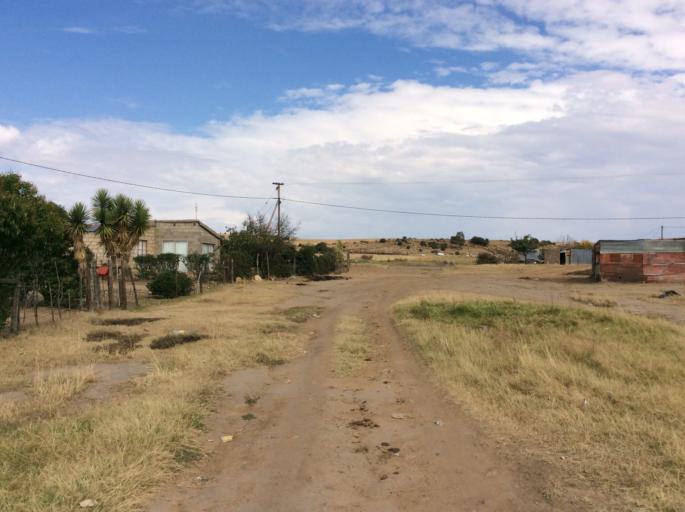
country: ZA
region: Orange Free State
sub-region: Xhariep District Municipality
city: Dewetsdorp
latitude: -29.5803
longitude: 26.6909
